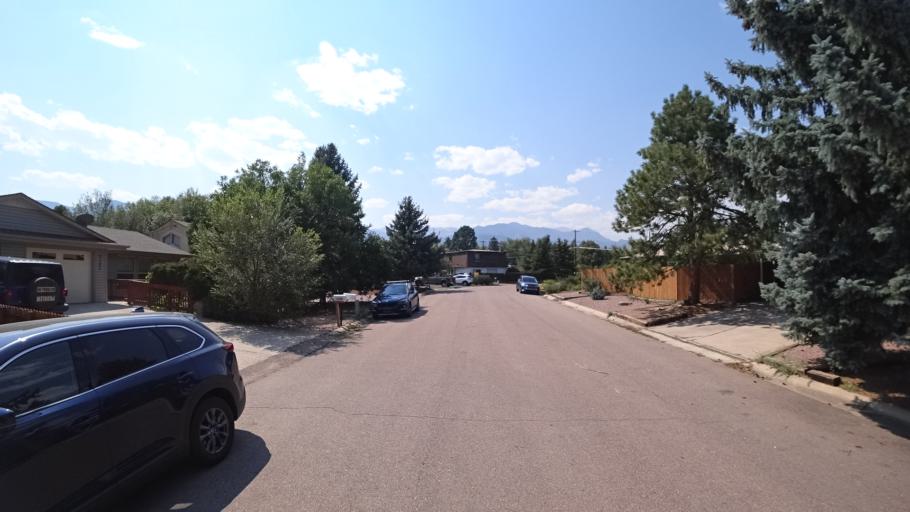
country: US
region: Colorado
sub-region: El Paso County
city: Colorado Springs
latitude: 38.8008
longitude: -104.8260
